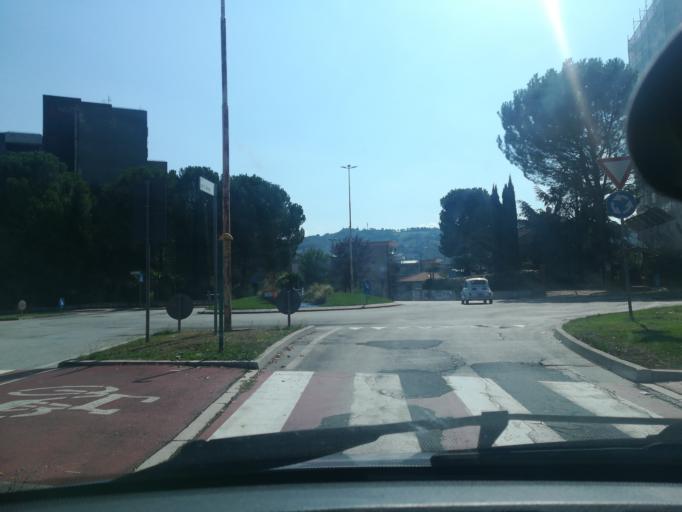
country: IT
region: The Marches
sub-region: Provincia di Macerata
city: Tolentino
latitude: 43.2147
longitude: 13.2987
